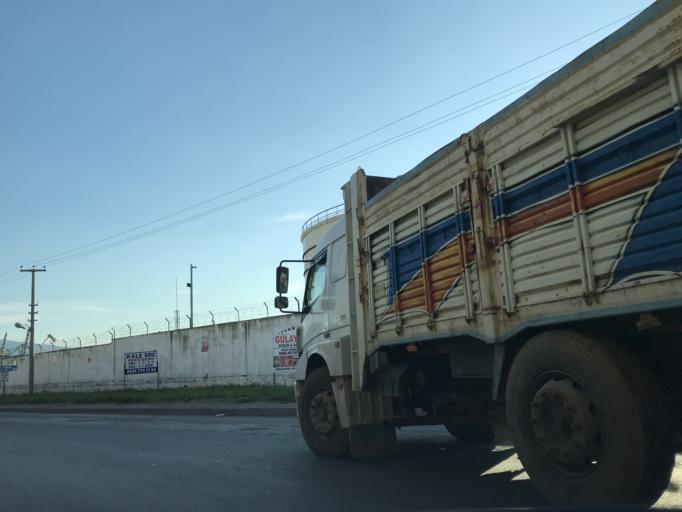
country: TR
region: Hatay
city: Iskenderun
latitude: 36.6088
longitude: 36.2007
